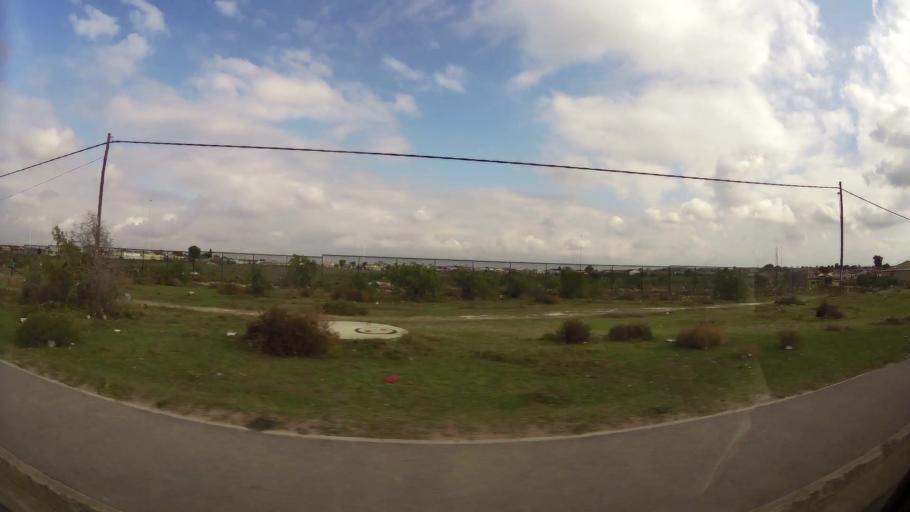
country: ZA
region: Eastern Cape
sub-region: Nelson Mandela Bay Metropolitan Municipality
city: Port Elizabeth
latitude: -33.8047
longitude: 25.5894
